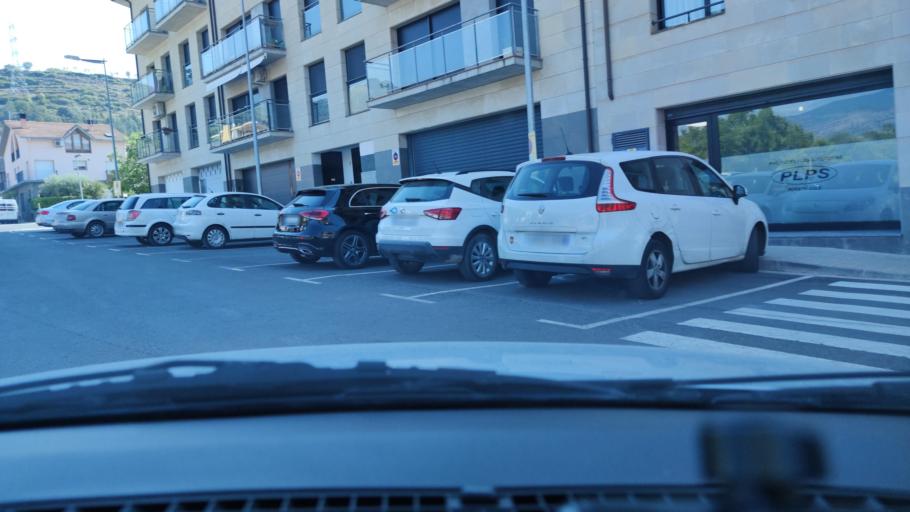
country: ES
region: Catalonia
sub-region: Provincia de Lleida
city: Senterada
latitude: 42.2510
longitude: 0.9642
